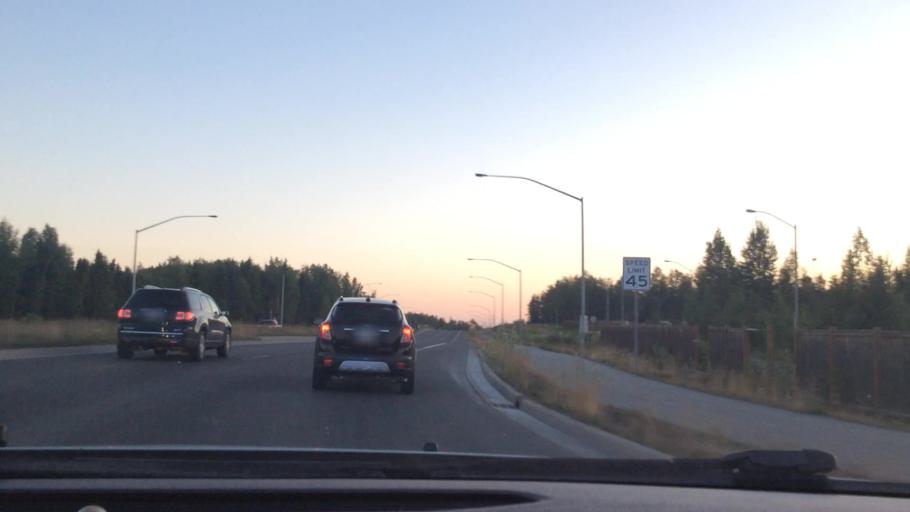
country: US
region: Alaska
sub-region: Anchorage Municipality
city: Anchorage
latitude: 61.1795
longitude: -149.7800
